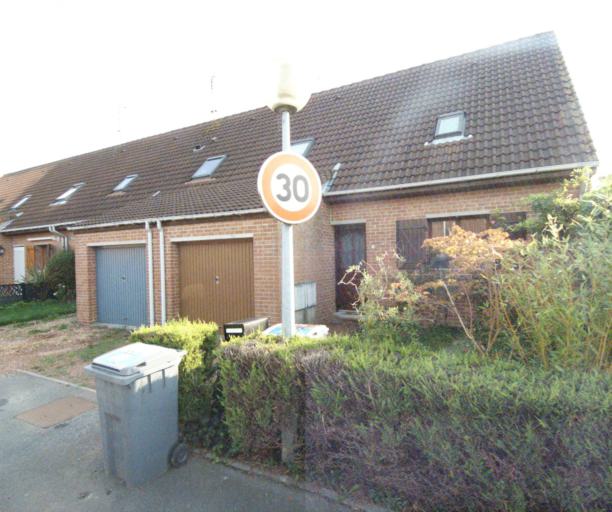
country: FR
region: Nord-Pas-de-Calais
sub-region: Departement du Nord
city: Perenchies
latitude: 50.6603
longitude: 2.9780
